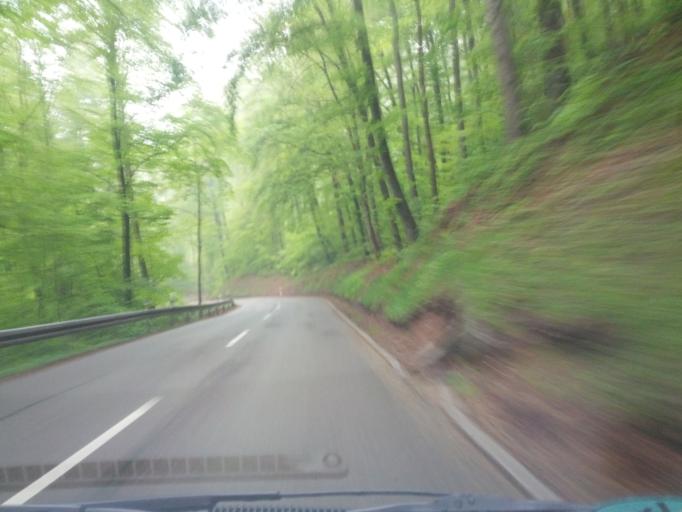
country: DE
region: Baden-Wuerttemberg
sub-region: Freiburg Region
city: Wehr
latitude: 47.6192
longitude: 7.9279
